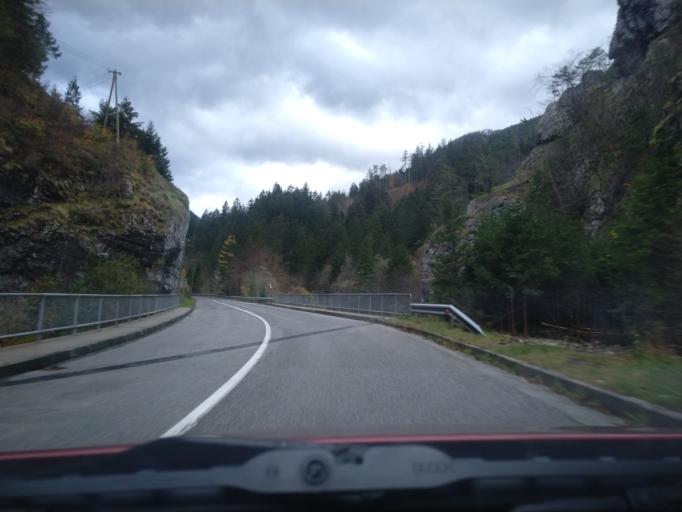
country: SI
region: Luce
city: Luce
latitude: 46.3829
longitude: 14.7256
